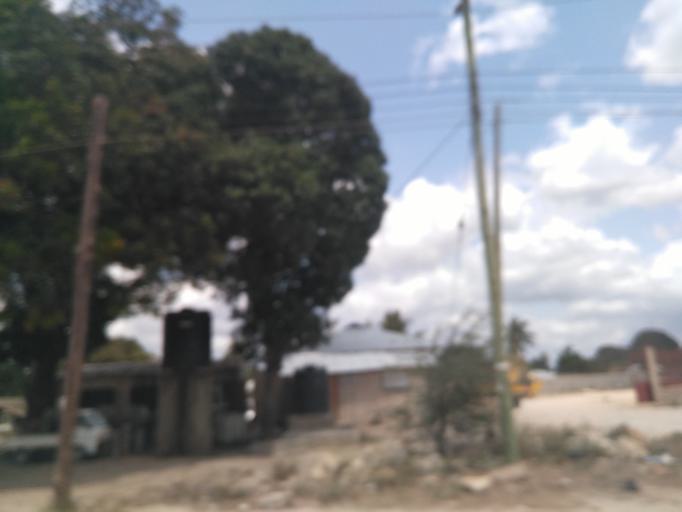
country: TZ
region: Dar es Salaam
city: Dar es Salaam
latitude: -6.8766
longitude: 39.3427
